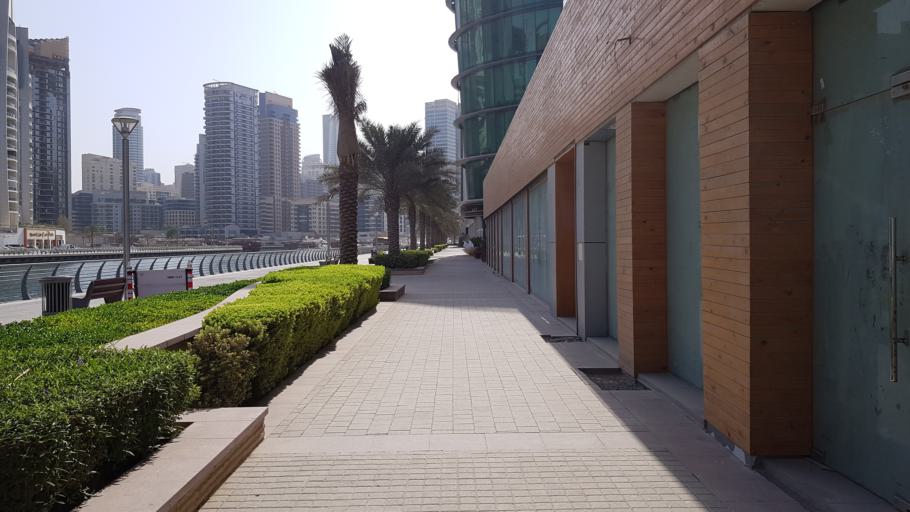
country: AE
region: Dubai
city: Dubai
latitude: 25.0705
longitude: 55.1273
